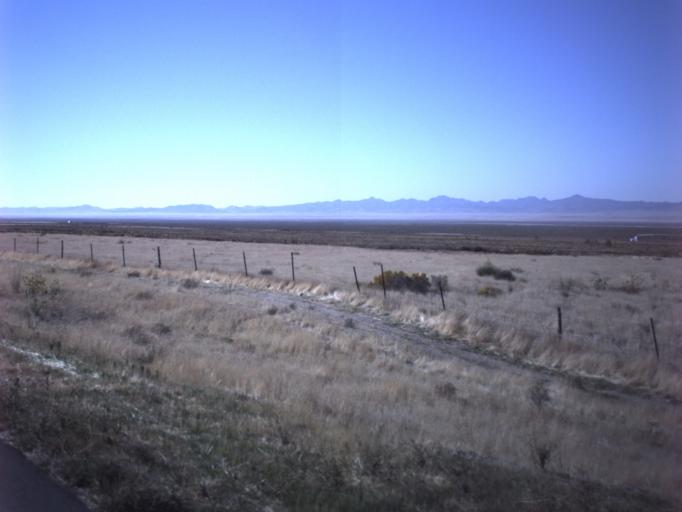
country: US
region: Utah
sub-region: Tooele County
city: Grantsville
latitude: 40.5215
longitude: -112.7477
